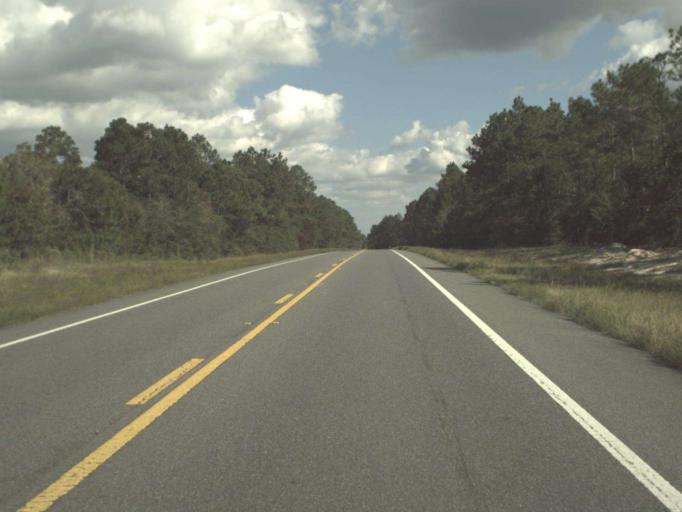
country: US
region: Florida
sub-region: Bay County
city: Laguna Beach
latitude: 30.4424
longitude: -85.8226
